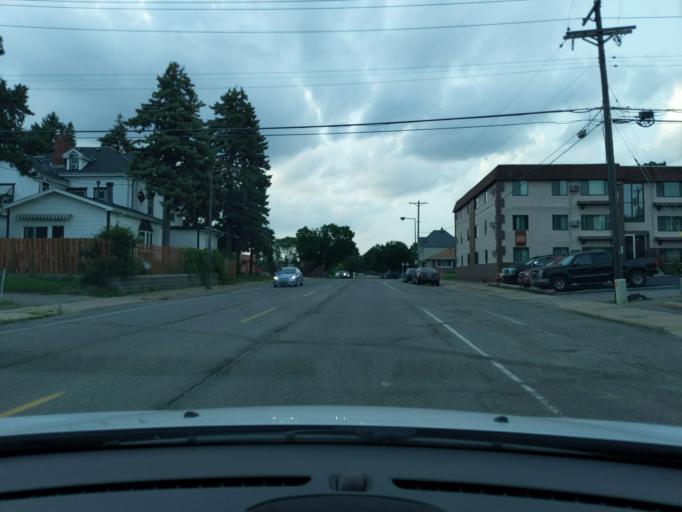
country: US
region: Minnesota
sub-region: Ramsey County
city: Falcon Heights
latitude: 44.9487
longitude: -93.1827
